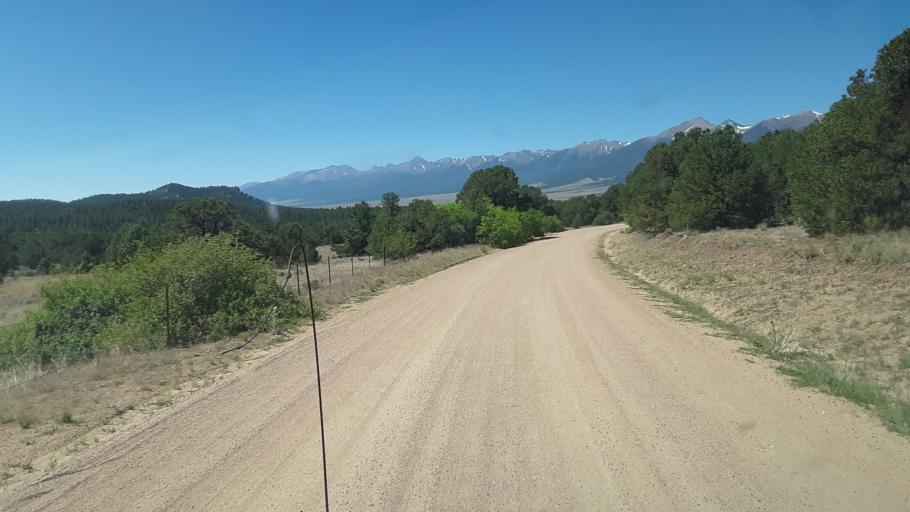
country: US
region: Colorado
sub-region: Custer County
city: Westcliffe
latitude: 38.2634
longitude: -105.5469
